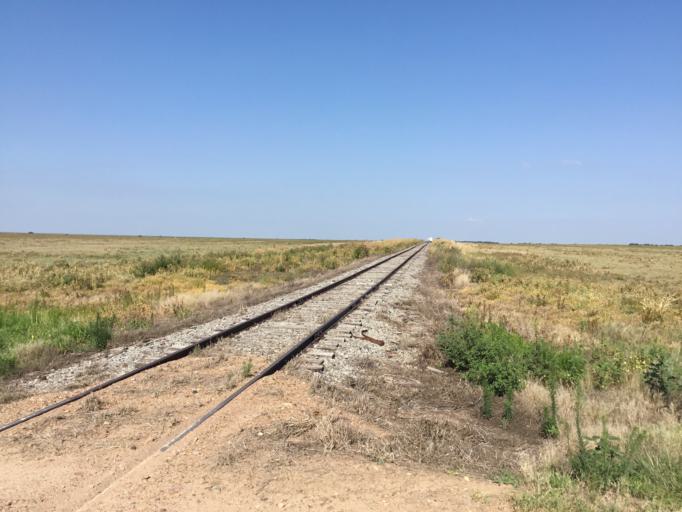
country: US
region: Kansas
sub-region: Pratt County
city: Pratt
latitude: 37.5101
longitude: -98.7754
